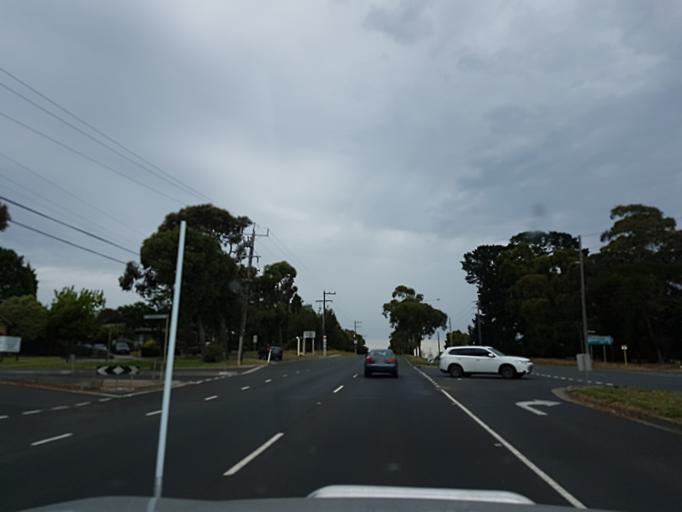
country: AU
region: Victoria
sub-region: Knox
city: Wantirna
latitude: -37.8498
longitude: 145.2345
